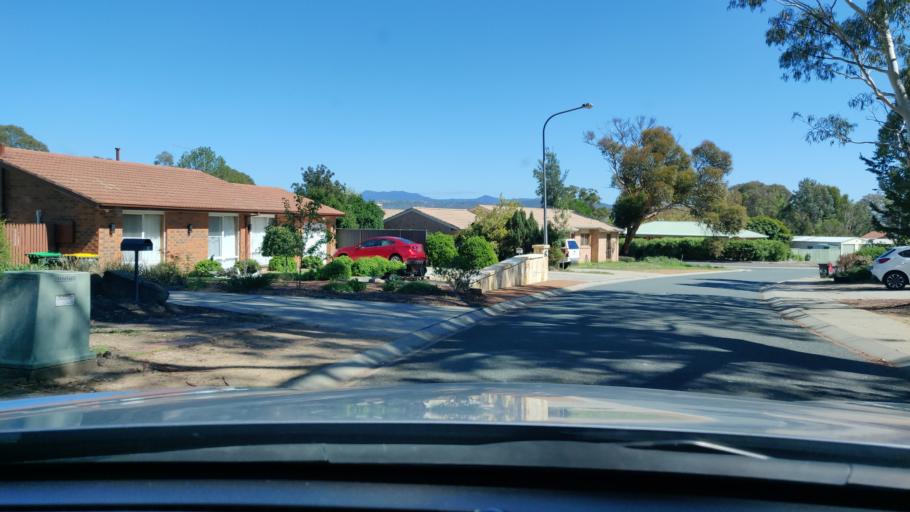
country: AU
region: Australian Capital Territory
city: Macarthur
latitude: -35.4420
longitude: 149.0992
